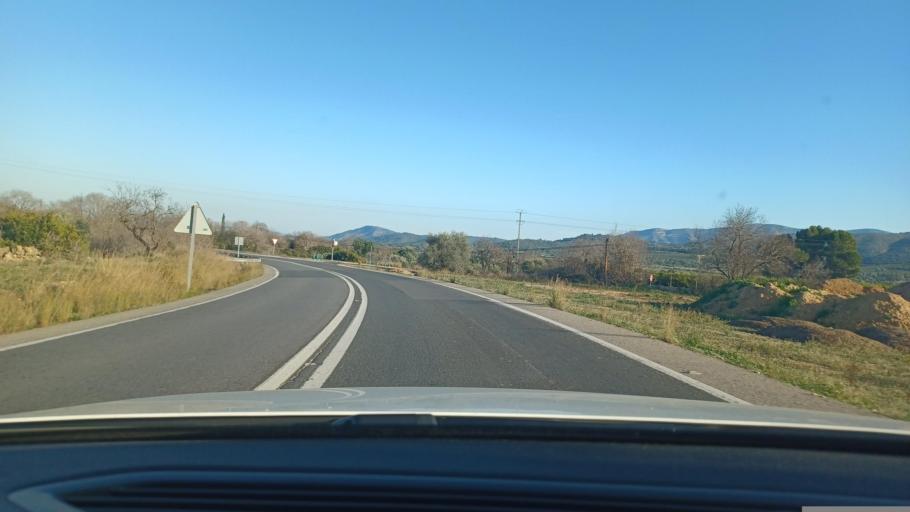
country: ES
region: Catalonia
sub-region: Provincia de Tarragona
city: Santa Barbara
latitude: 40.6855
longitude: 0.4665
